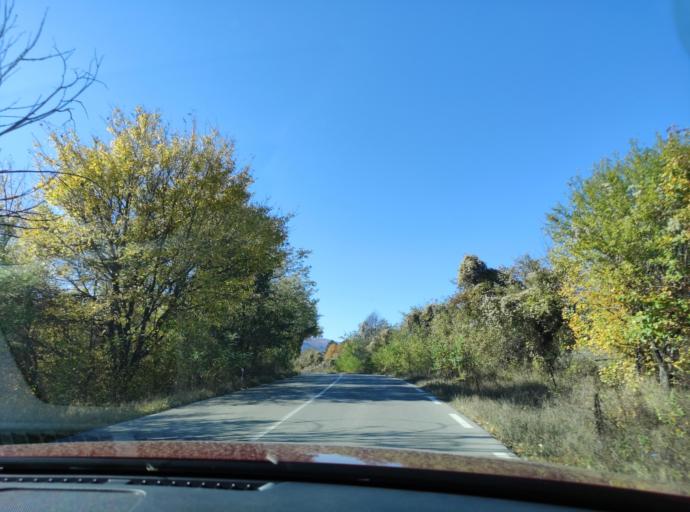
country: BG
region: Montana
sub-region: Obshtina Chiprovtsi
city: Chiprovtsi
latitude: 43.4320
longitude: 22.9895
